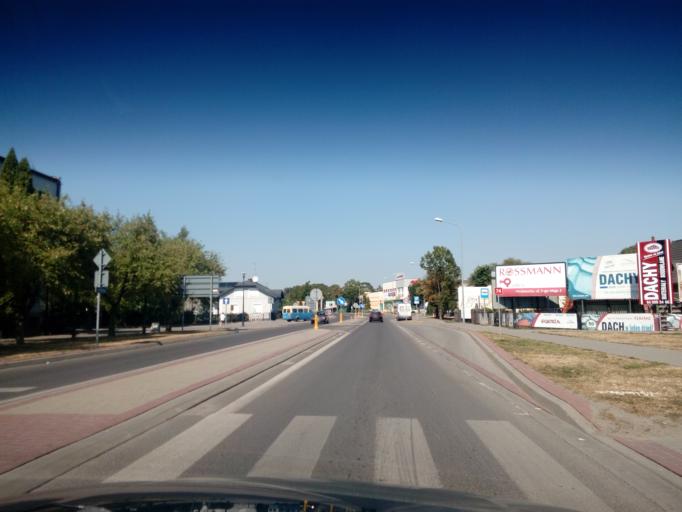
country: PL
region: Lublin Voivodeship
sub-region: Powiat hrubieszowski
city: Hrubieszow
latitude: 50.7966
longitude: 23.9034
